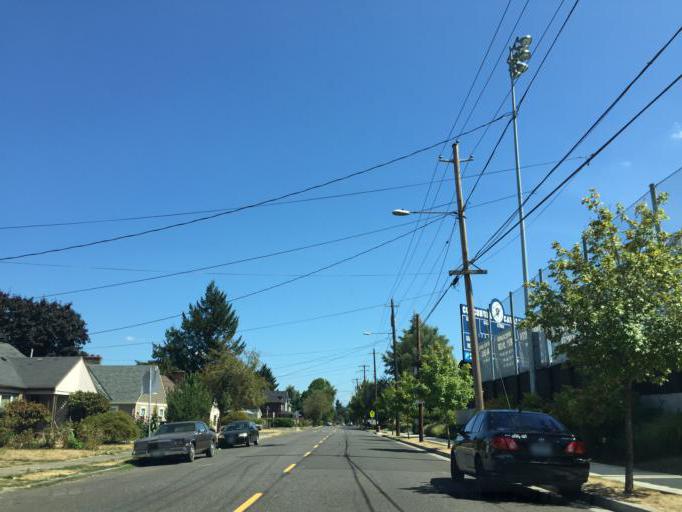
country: US
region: Oregon
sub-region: Multnomah County
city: Portland
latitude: 45.5719
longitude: -122.6373
